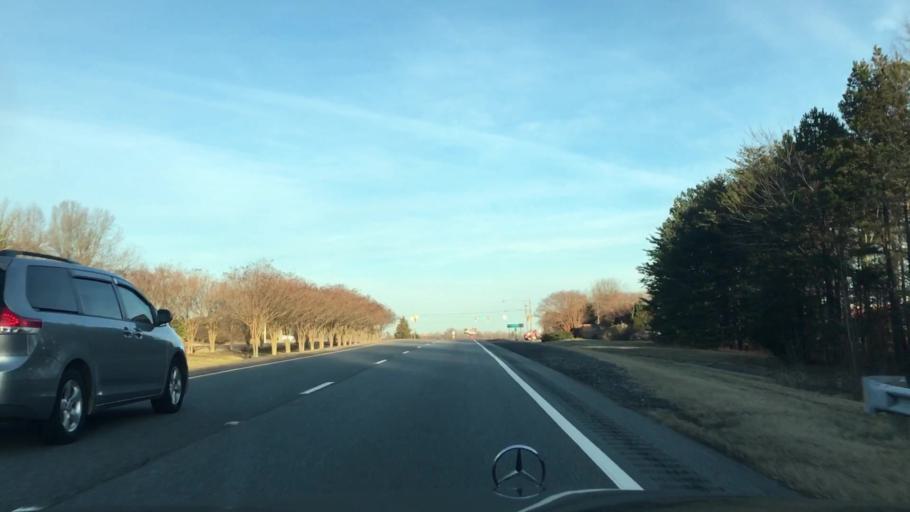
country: US
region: North Carolina
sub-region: Guilford County
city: Greensboro
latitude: 36.0265
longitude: -79.7685
